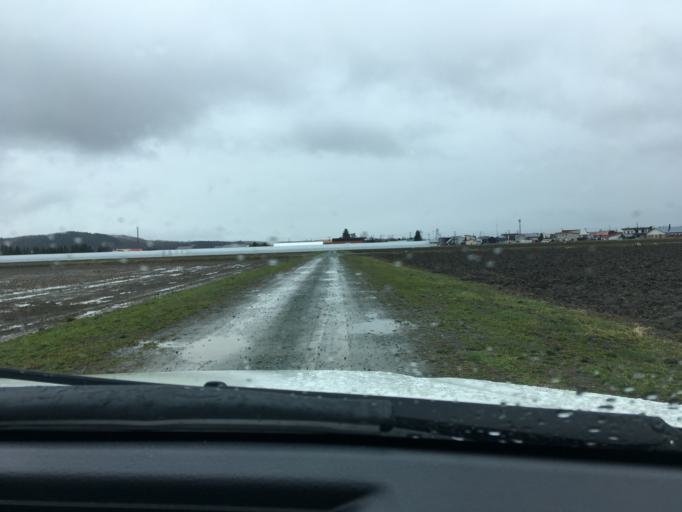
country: JP
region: Hokkaido
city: Nayoro
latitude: 44.1325
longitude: 142.4917
